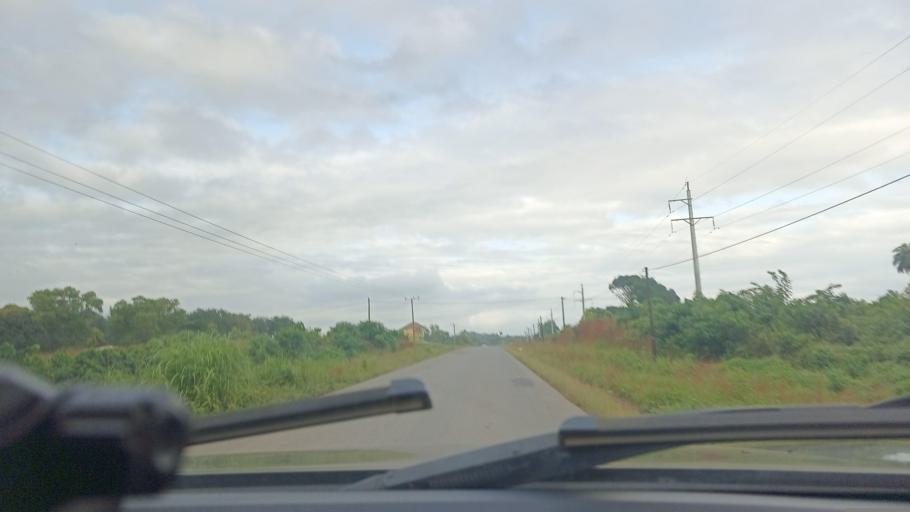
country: LR
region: Montserrado
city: Monrovia
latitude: 6.5700
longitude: -10.8777
